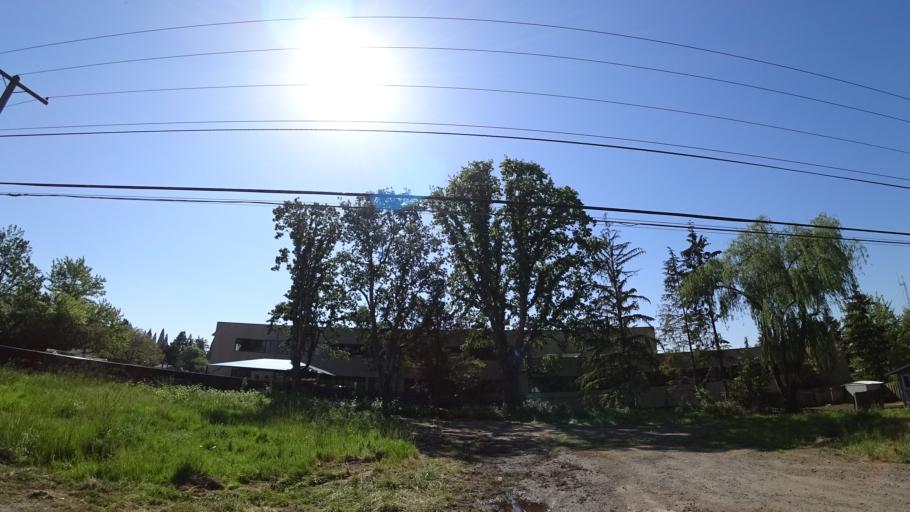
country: US
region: Oregon
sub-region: Washington County
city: Beaverton
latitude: 45.4914
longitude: -122.8247
